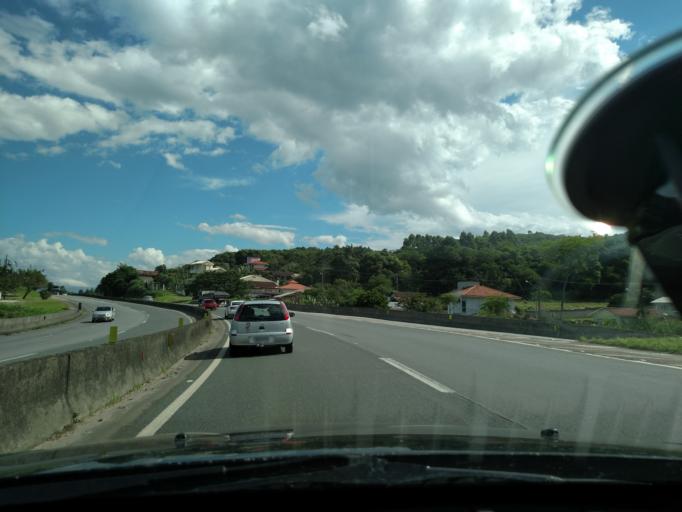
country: BR
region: Santa Catarina
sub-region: Biguacu
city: Biguacu
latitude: -27.4334
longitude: -48.6251
